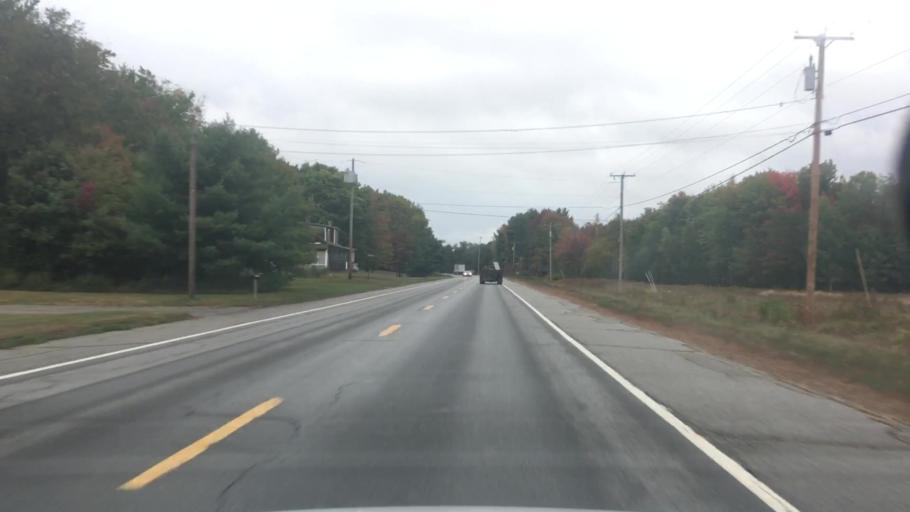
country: US
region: Maine
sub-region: Kennebec County
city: Belgrade
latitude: 44.4379
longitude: -69.8325
